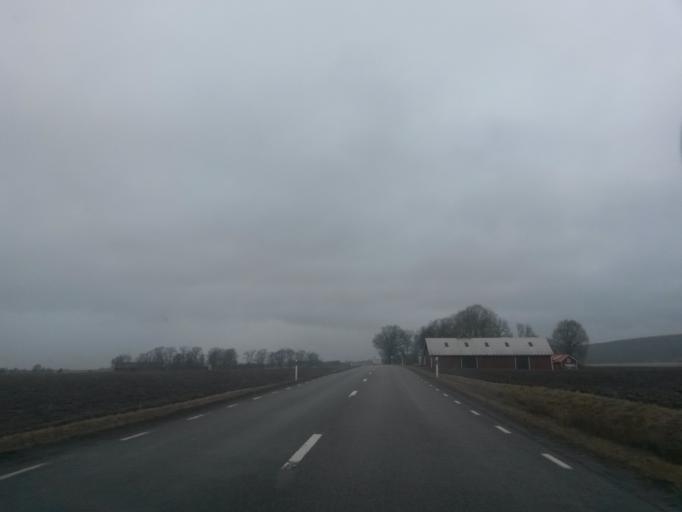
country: SE
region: Vaestra Goetaland
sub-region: Vanersborgs Kommun
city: Vargon
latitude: 58.2749
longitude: 12.3992
